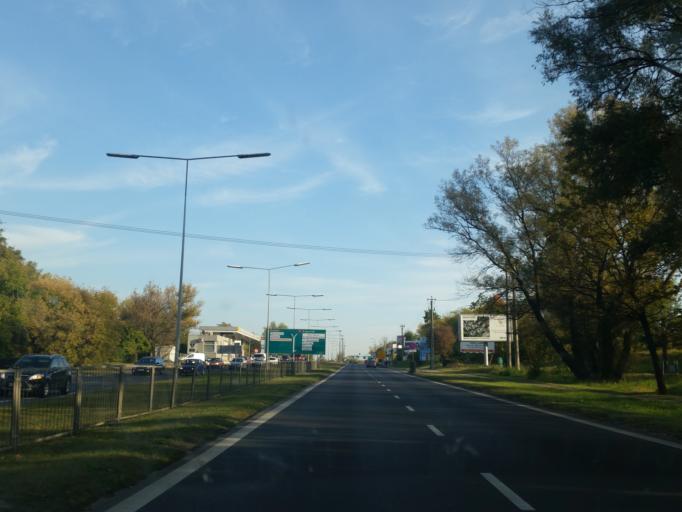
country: PL
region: Masovian Voivodeship
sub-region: Warszawa
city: Bielany
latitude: 52.3085
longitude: 20.9281
